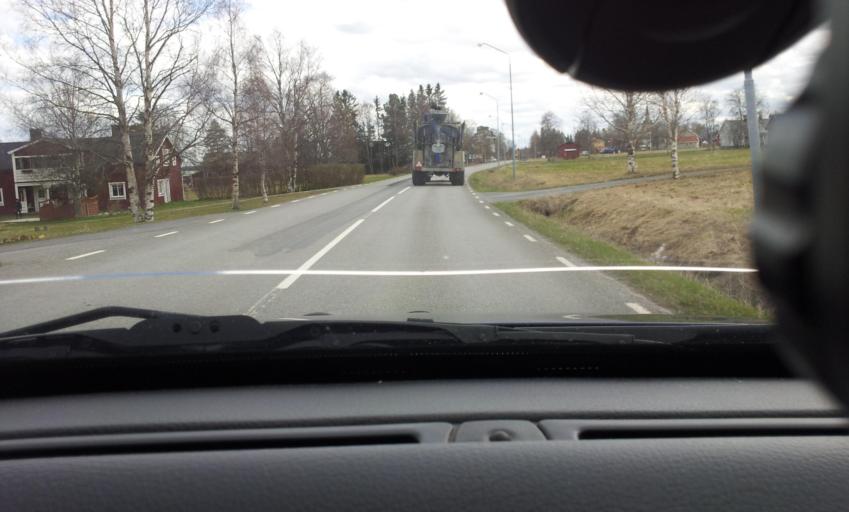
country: SE
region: Jaemtland
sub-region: OEstersunds Kommun
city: Brunflo
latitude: 63.1148
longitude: 14.7274
